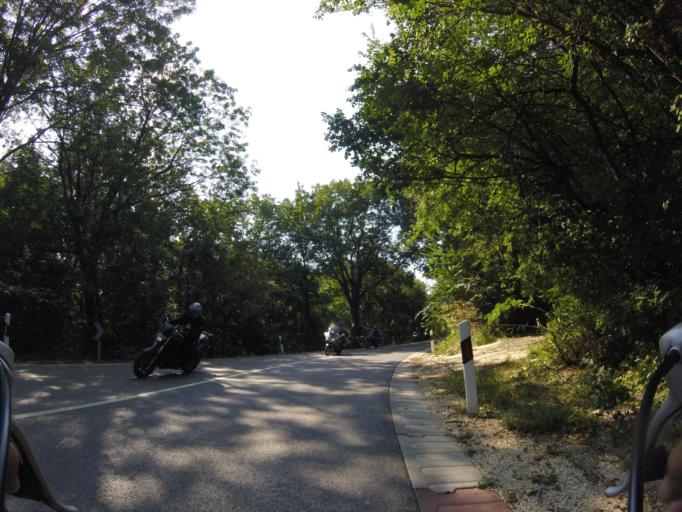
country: HU
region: Komarom-Esztergom
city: Nyergesujfalu
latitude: 47.7014
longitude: 18.5577
